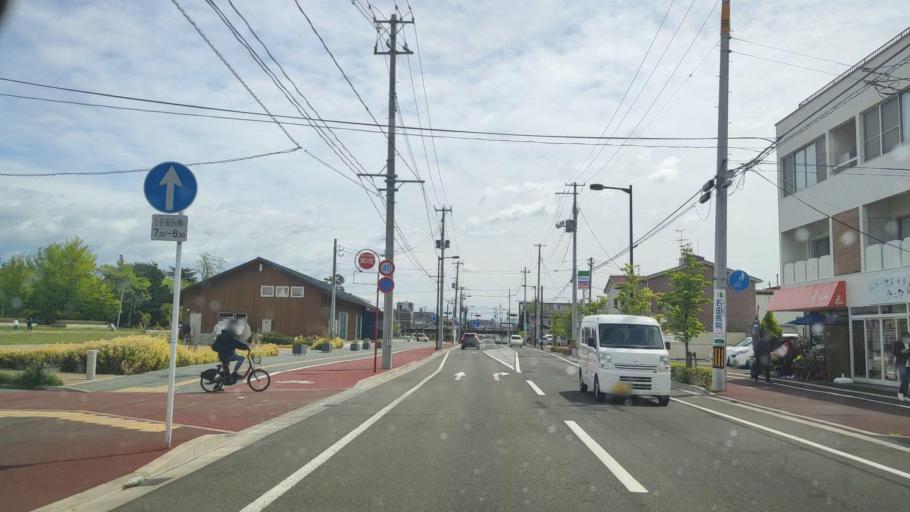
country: JP
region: Miyagi
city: Sendai-shi
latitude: 38.2496
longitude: 140.9014
